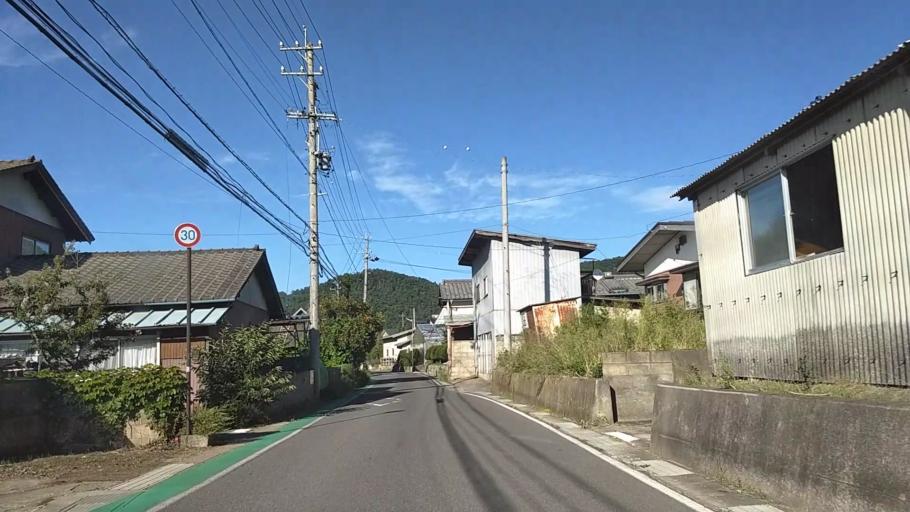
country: JP
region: Nagano
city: Nagano-shi
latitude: 36.5490
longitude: 138.1549
